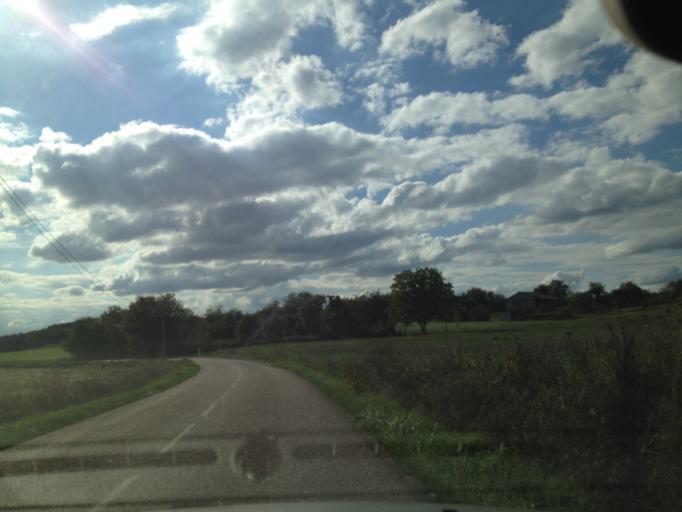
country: FR
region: Franche-Comte
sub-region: Departement de la Haute-Saone
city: Faverney
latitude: 47.7992
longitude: 6.0498
